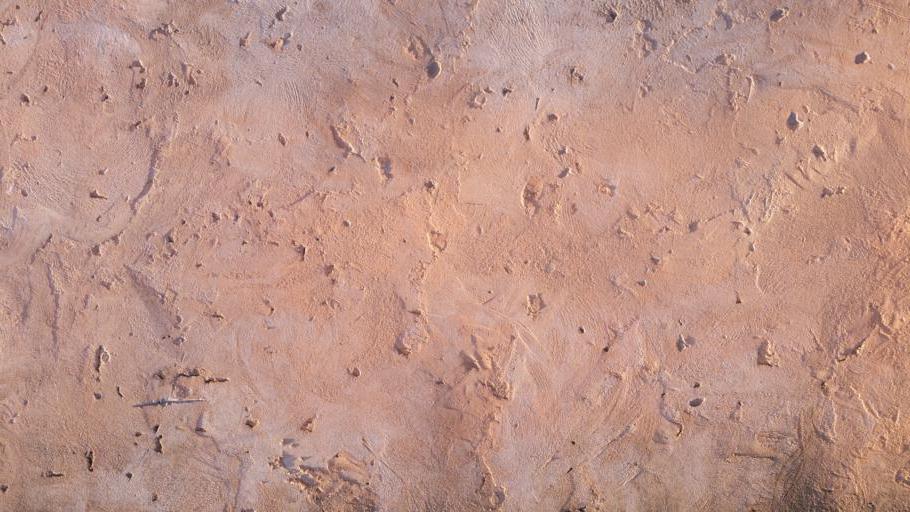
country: MA
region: Marrakech-Tensift-Al Haouz
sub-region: Marrakech
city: Marrakesh
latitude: 31.6552
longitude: -7.9799
